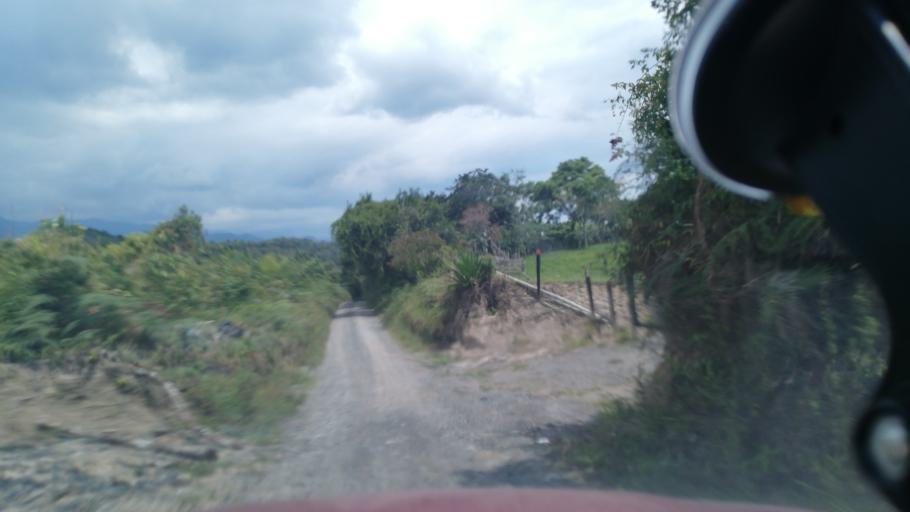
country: CO
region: Cundinamarca
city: Vergara
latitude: 5.1912
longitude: -74.2747
